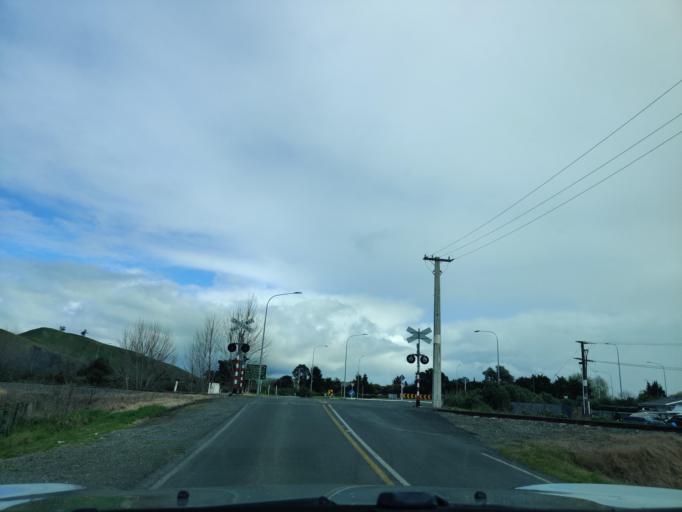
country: NZ
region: Hawke's Bay
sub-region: Hastings District
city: Hastings
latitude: -39.6914
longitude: 176.7950
